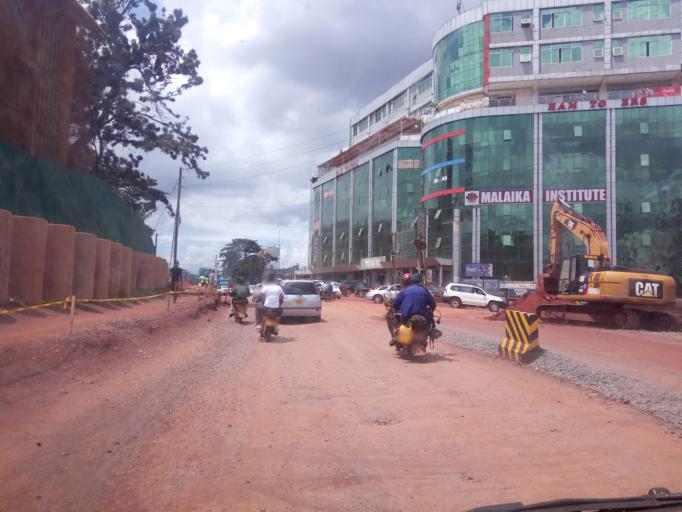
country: UG
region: Central Region
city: Kampala Central Division
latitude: 0.3284
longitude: 32.5707
